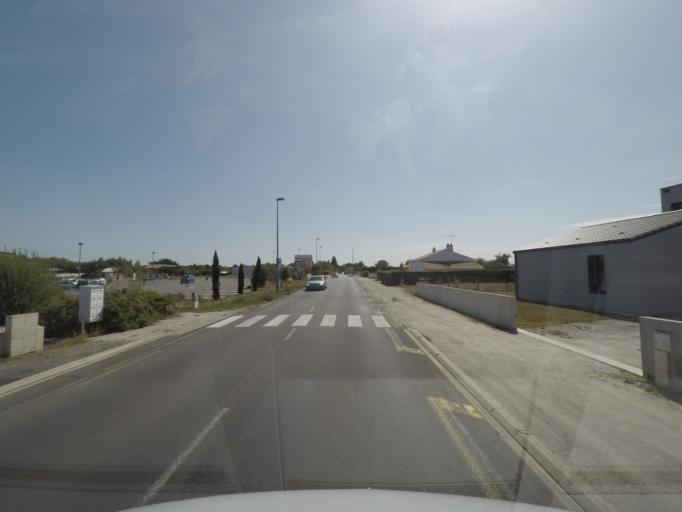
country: FR
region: Pays de la Loire
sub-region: Departement de la Vendee
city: Beauvoir-sur-Mer
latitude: 46.9093
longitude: -2.0314
